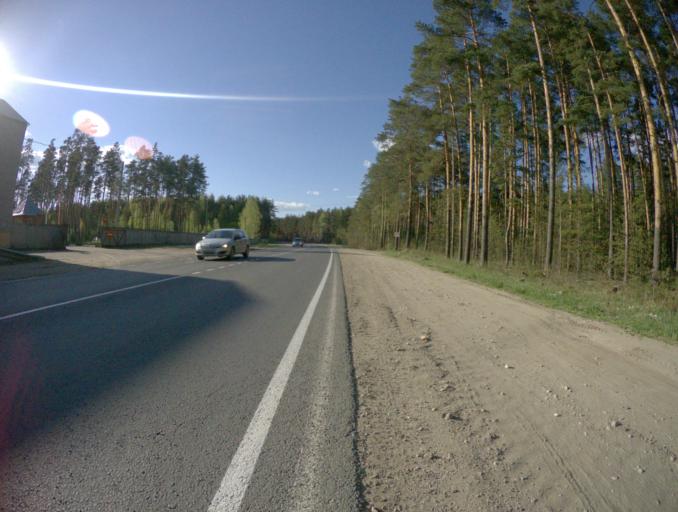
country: RU
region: Vladimir
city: Raduzhnyy
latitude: 56.0277
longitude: 40.3794
